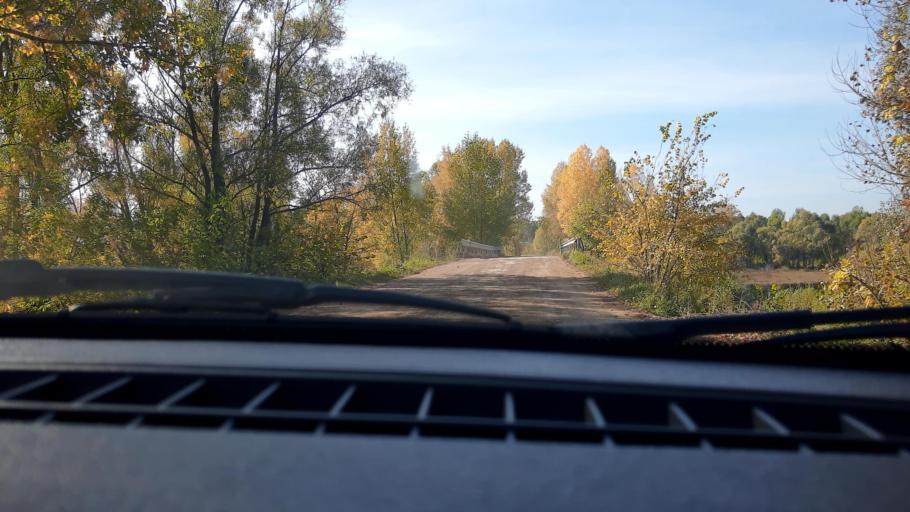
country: RU
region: Bashkortostan
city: Mikhaylovka
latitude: 54.7379
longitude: 55.8380
